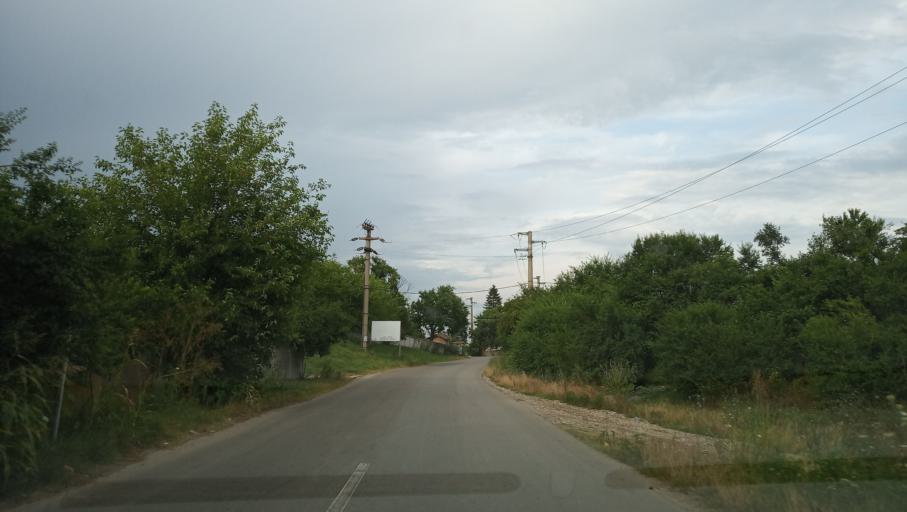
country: RO
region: Giurgiu
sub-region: Comuna Singureni
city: Singureni
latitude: 44.2323
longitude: 25.9399
